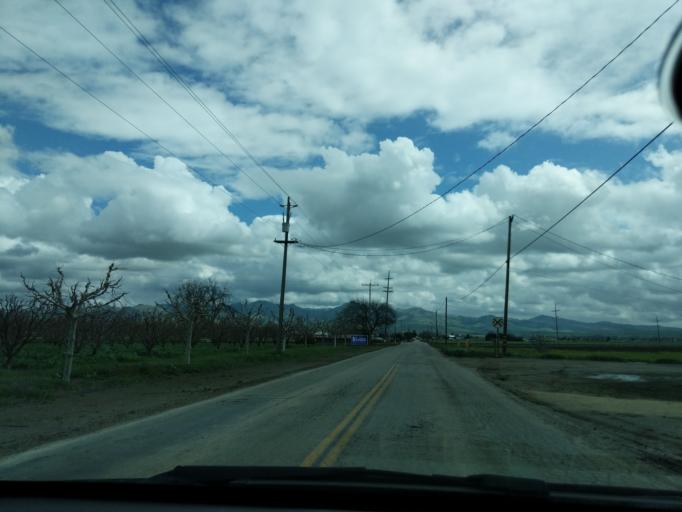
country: US
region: California
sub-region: San Benito County
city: Hollister
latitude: 36.8700
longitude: -121.4162
